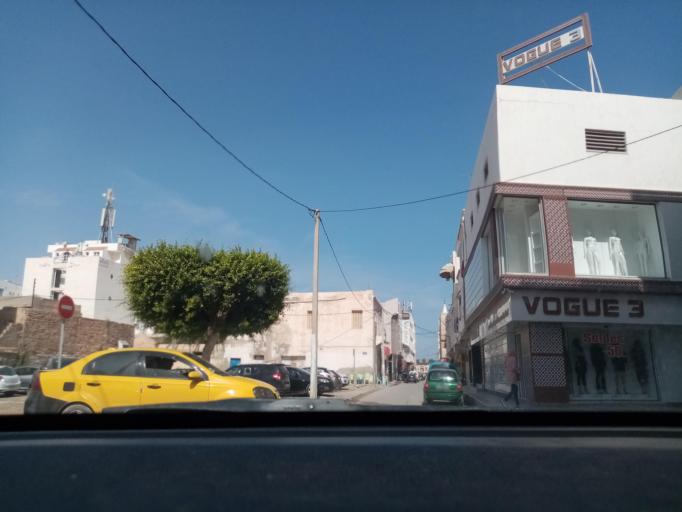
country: TN
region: Qabis
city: Gabes
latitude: 33.8863
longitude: 10.1045
